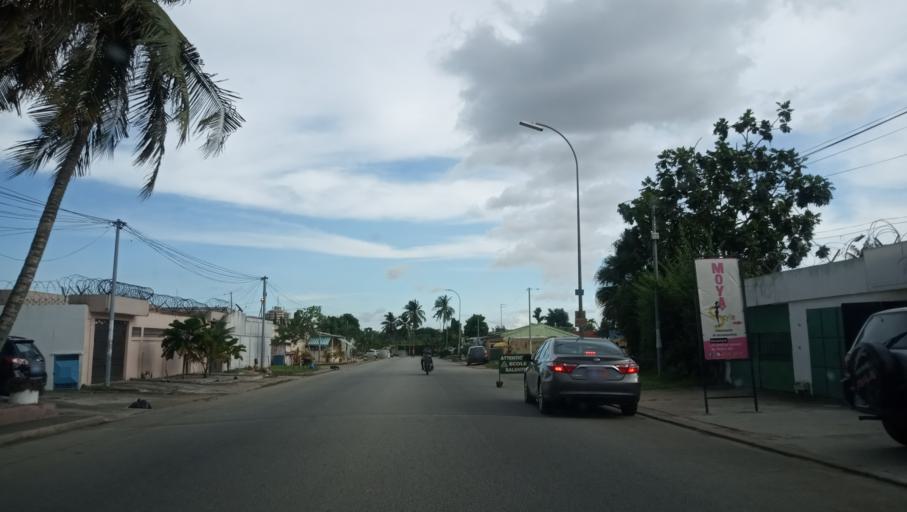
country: CI
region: Lagunes
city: Abidjan
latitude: 5.3462
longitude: -3.9801
